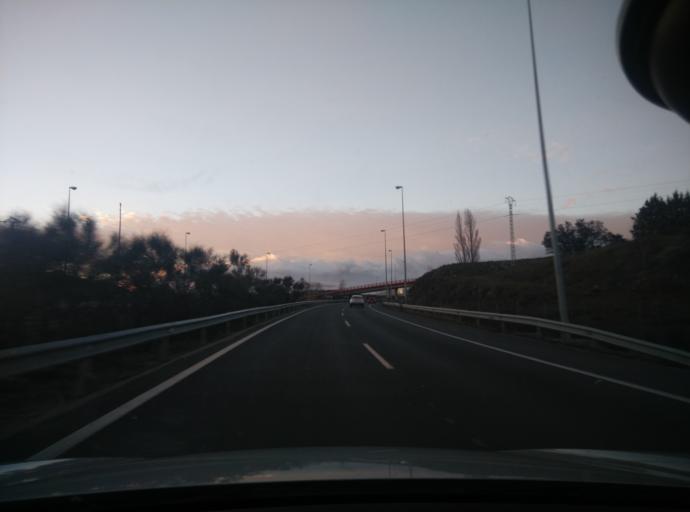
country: ES
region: Madrid
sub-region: Provincia de Madrid
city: Colmenar Viejo
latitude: 40.6559
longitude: -3.7454
